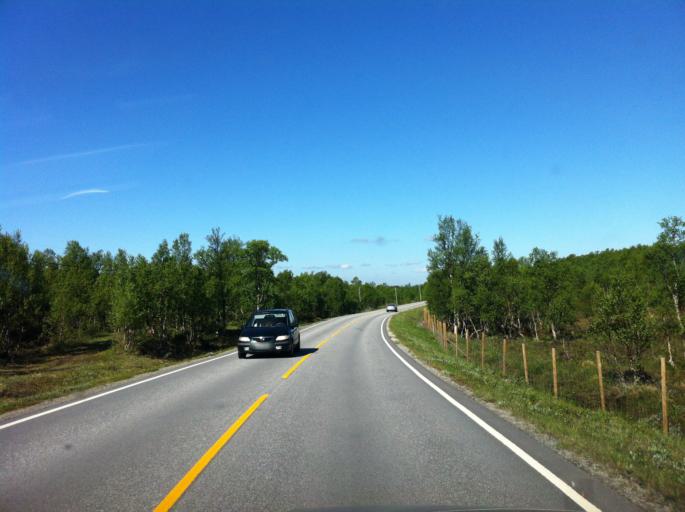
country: NO
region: Sor-Trondelag
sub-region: Tydal
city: Aas
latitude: 62.6350
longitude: 11.9339
